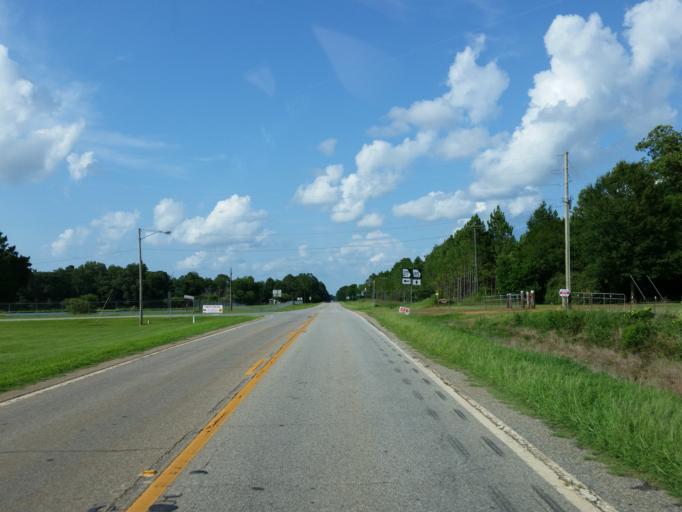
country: US
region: Georgia
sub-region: Lee County
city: Leesburg
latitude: 31.8191
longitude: -84.1102
